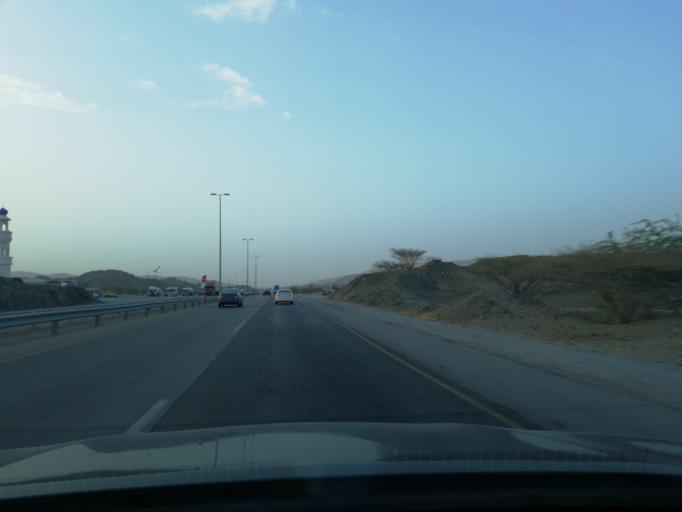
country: OM
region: Muhafazat ad Dakhiliyah
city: Bidbid
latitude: 23.5088
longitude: 58.1922
